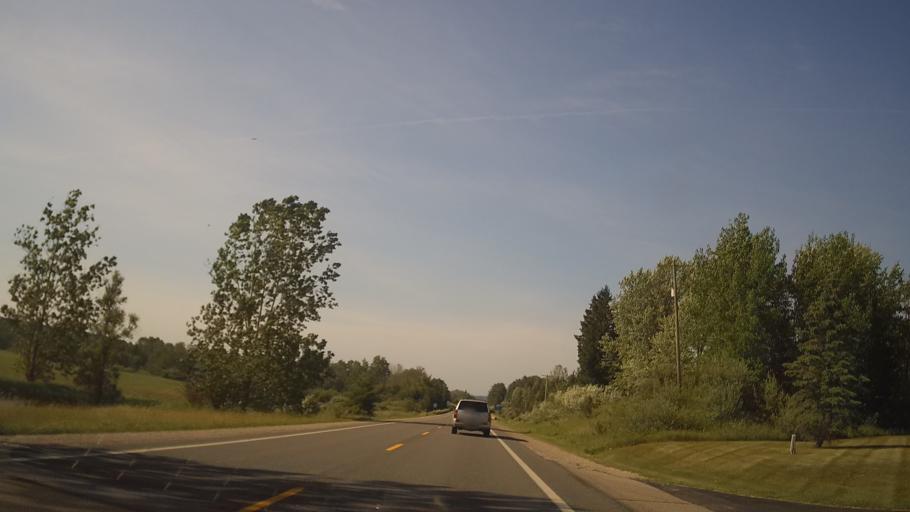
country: US
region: Michigan
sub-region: Ogemaw County
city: West Branch
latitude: 44.3883
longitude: -84.1162
